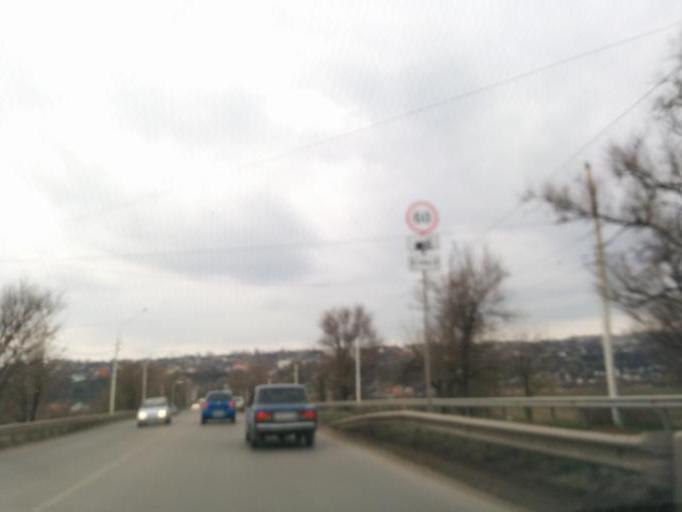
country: RU
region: Rostov
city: Novocherkassk
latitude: 47.4353
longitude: 40.0994
